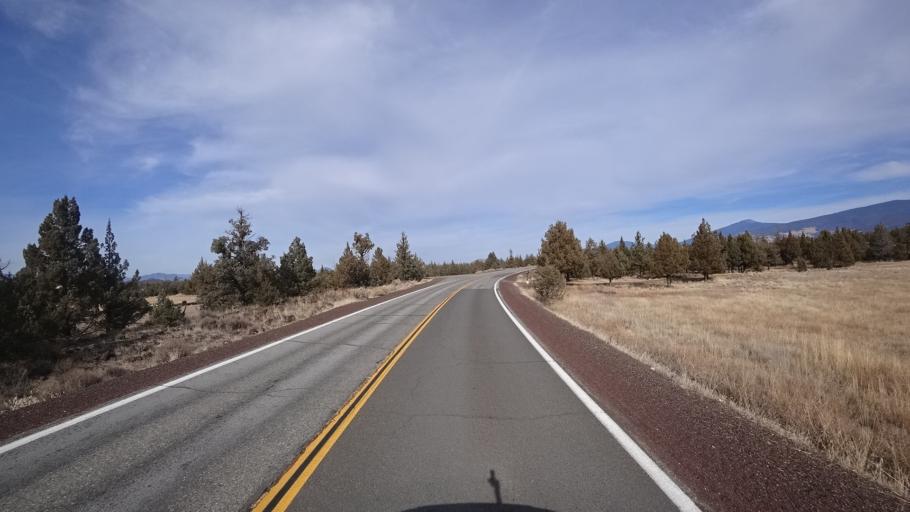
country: US
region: California
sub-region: Siskiyou County
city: Weed
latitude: 41.5900
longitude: -122.4002
